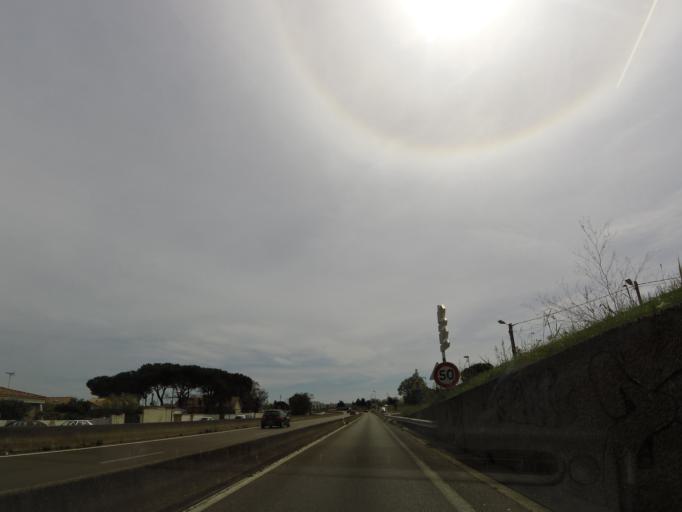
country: FR
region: Languedoc-Roussillon
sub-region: Departement de l'Herault
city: Perols
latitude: 43.5542
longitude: 3.9674
